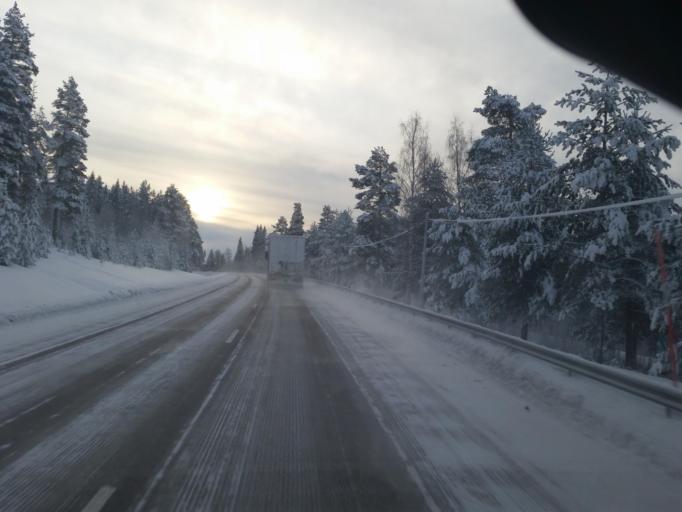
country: SE
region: Norrbotten
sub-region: Alvsbyns Kommun
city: AElvsbyn
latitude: 65.6612
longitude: 21.2201
